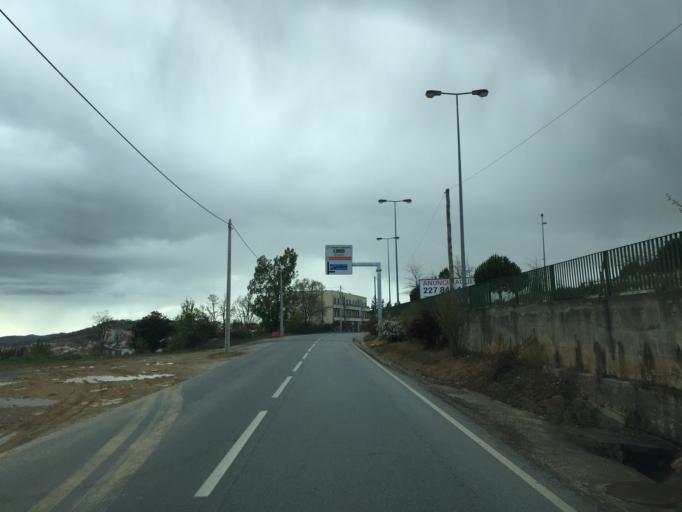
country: PT
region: Braganca
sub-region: Mogadouro
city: Mogadouro
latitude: 41.3420
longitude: -6.7019
